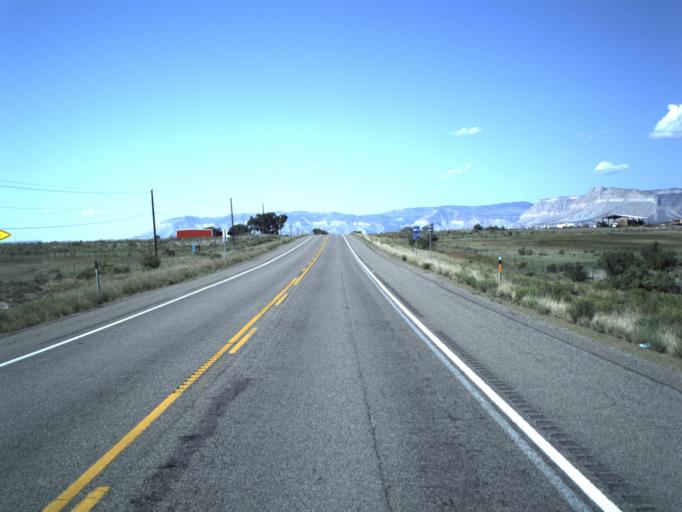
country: US
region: Utah
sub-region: Emery County
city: Castle Dale
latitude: 39.1894
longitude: -111.0268
